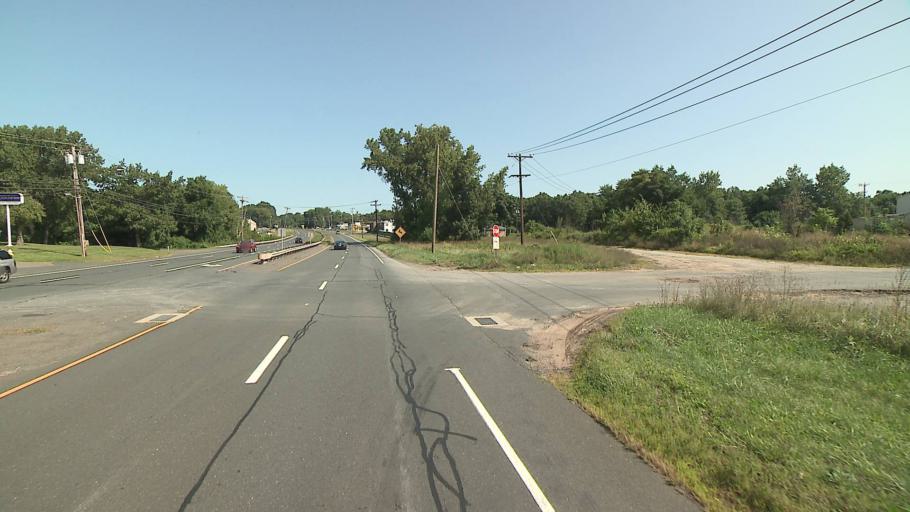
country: US
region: Connecticut
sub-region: Hartford County
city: South Windsor
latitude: 41.8457
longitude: -72.5996
